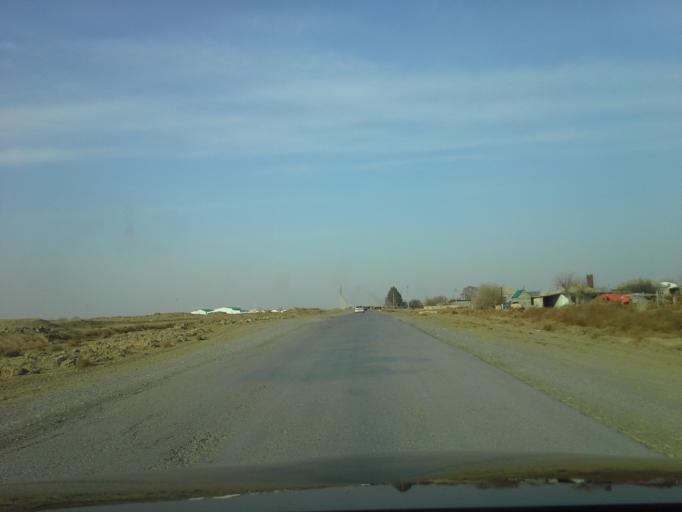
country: TM
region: Ahal
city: Abadan
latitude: 38.1759
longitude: 58.0380
